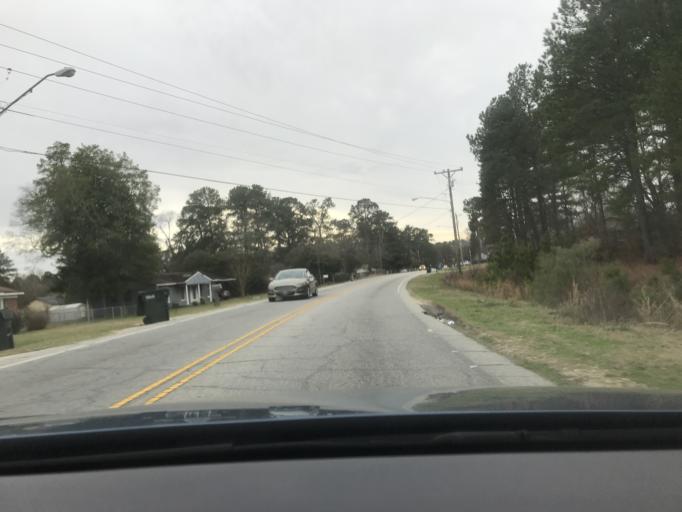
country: US
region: North Carolina
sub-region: Hoke County
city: Rockfish
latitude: 35.0323
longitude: -78.9978
